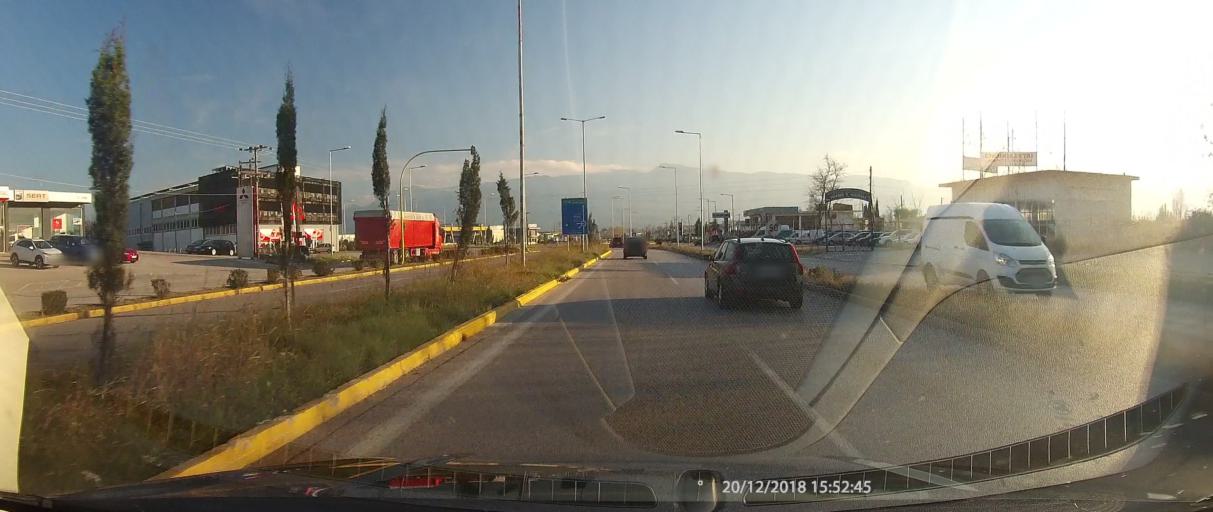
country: GR
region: Central Greece
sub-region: Nomos Fthiotidos
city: Rodhitsa
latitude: 38.8786
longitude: 22.4534
